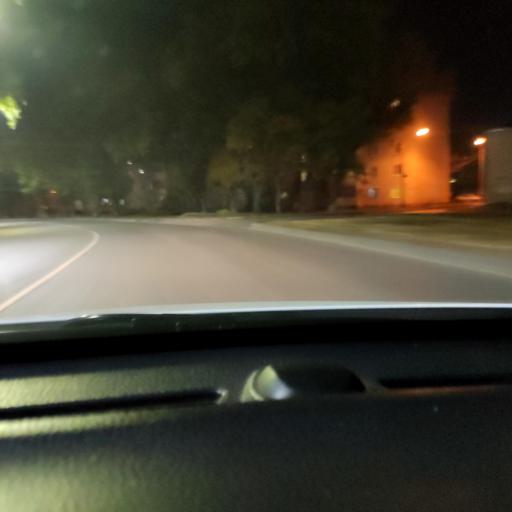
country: RU
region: Voronezj
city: Somovo
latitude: 51.7188
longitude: 39.2738
